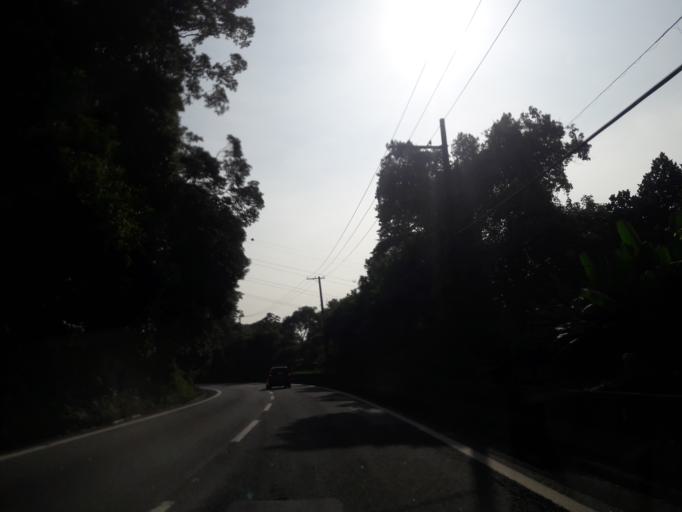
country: BR
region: Sao Paulo
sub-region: Cubatao
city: Cubatao
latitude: -23.8887
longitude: -46.4647
